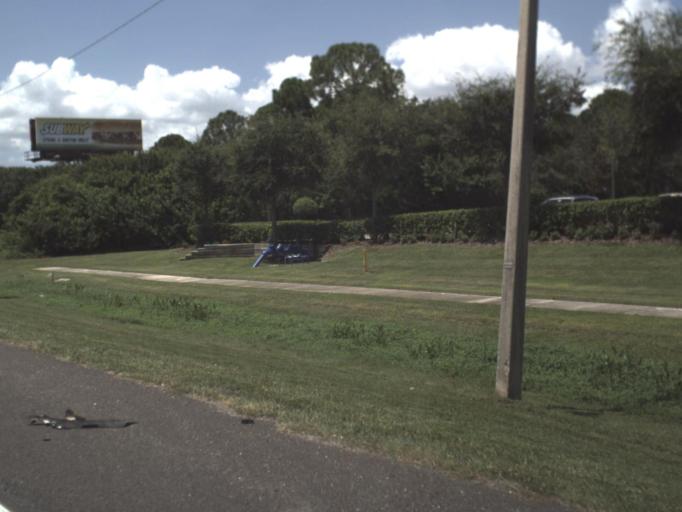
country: US
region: Florida
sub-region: Pinellas County
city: South Highpoint
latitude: 27.8940
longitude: -82.6885
